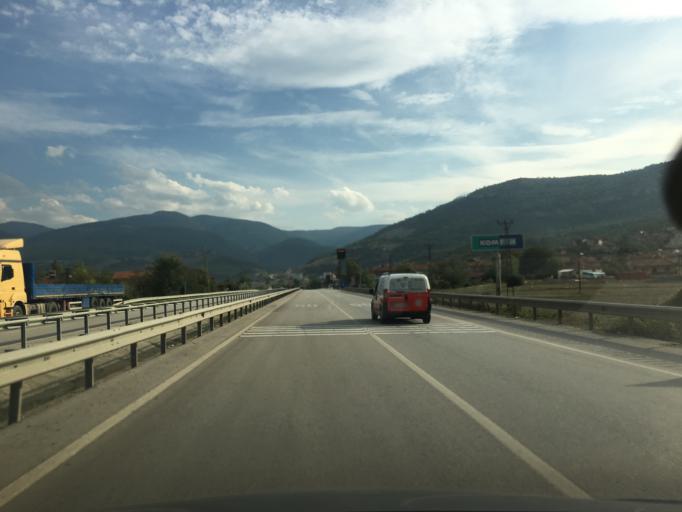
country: TR
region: Karabuk
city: Karabuk
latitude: 41.1066
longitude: 32.6688
